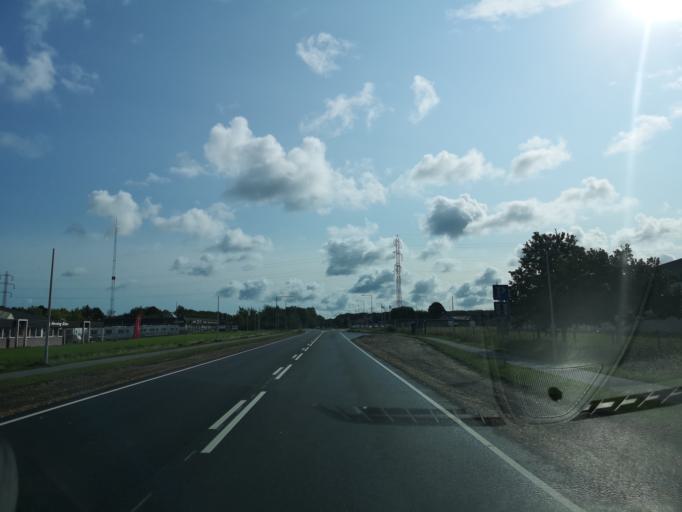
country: DK
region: Central Jutland
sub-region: Herning Kommune
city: Snejbjerg
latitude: 56.1348
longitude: 8.9274
